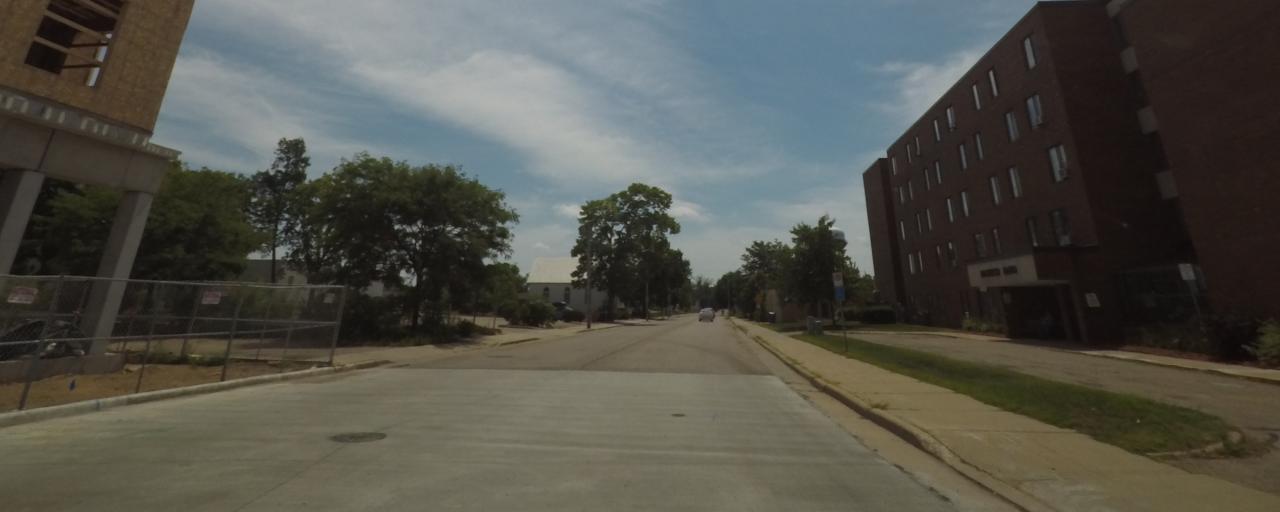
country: US
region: Wisconsin
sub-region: Portage County
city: Stevens Point
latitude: 44.5212
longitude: -89.5846
